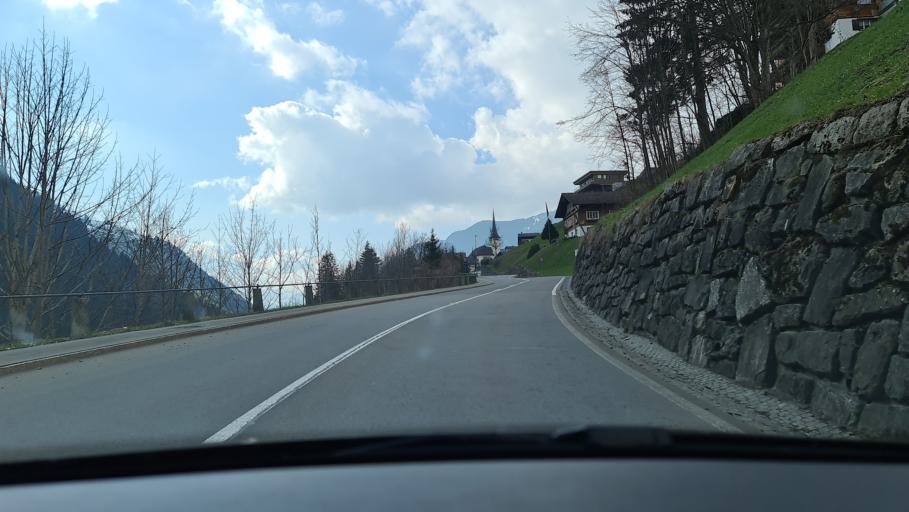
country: CH
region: Uri
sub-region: Uri
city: Burglen
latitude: 46.8706
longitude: 8.7327
